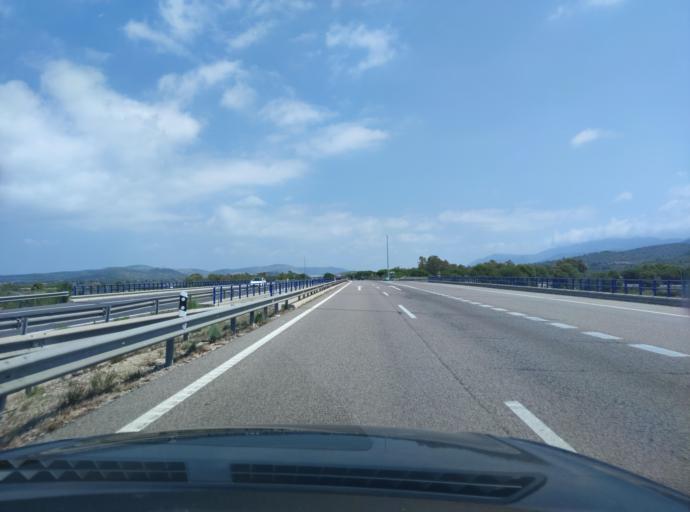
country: ES
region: Catalonia
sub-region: Provincia de Tarragona
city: Ulldecona
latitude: 40.5546
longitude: 0.4248
